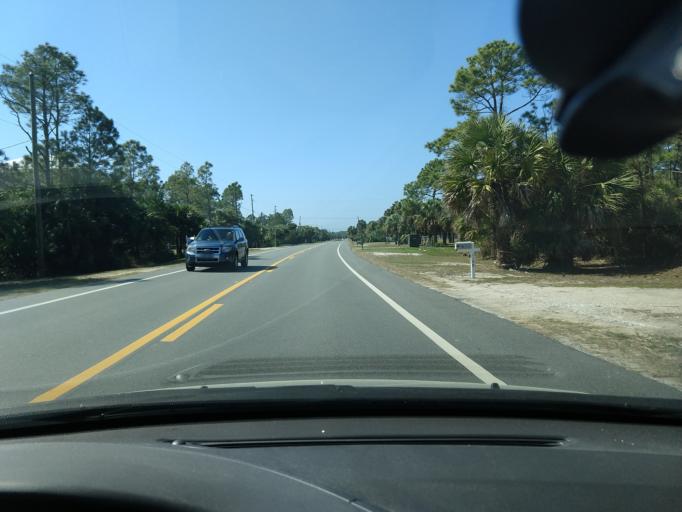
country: US
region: Florida
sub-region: Gulf County
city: Port Saint Joe
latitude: 29.6803
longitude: -85.2422
